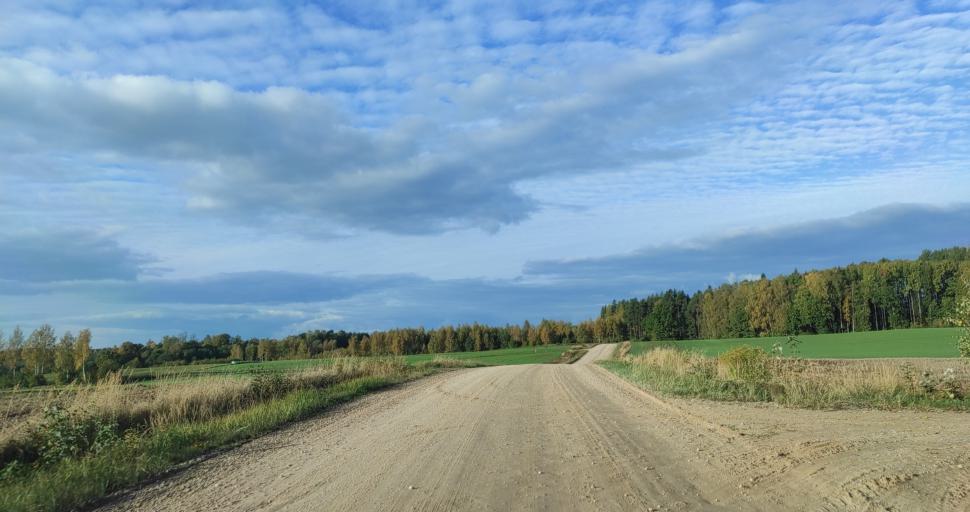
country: LV
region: Skrunda
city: Skrunda
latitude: 56.7437
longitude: 21.8651
